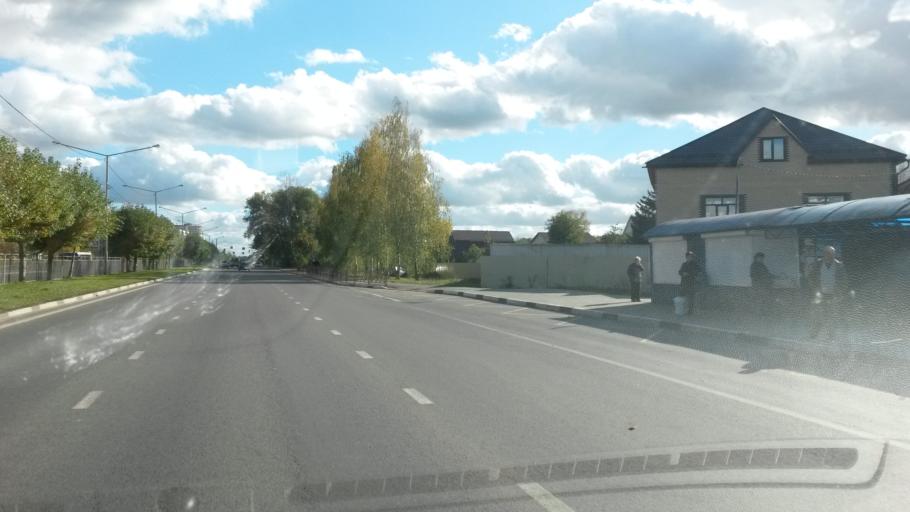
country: RU
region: Jaroslavl
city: Yaroslavl
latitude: 57.5733
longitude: 39.9202
